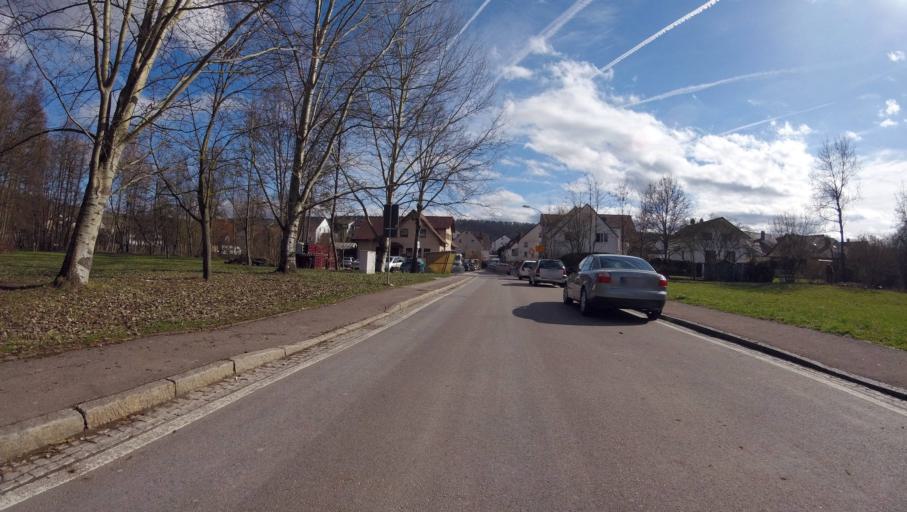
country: DE
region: Baden-Wuerttemberg
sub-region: Regierungsbezirk Stuttgart
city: Oberstenfeld
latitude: 49.0111
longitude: 9.3105
